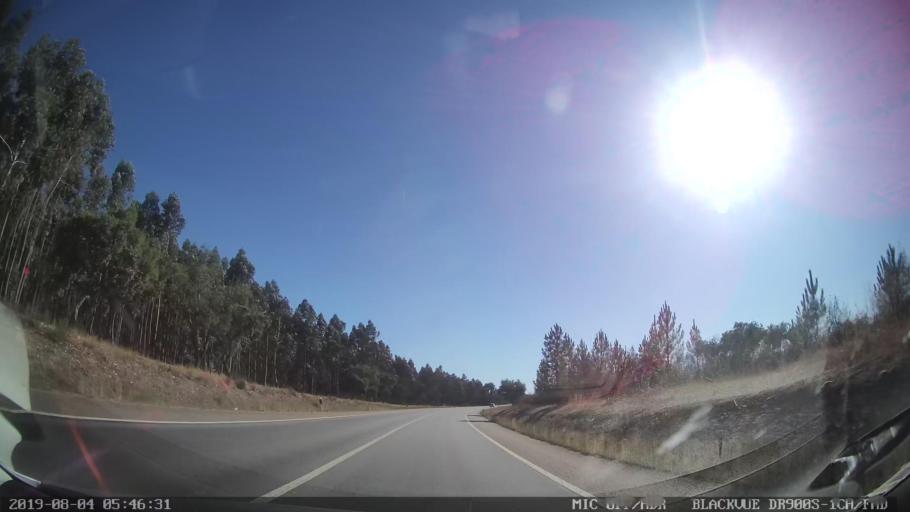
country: PT
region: Portalegre
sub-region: Gaviao
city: Gaviao
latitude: 39.4496
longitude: -7.7891
